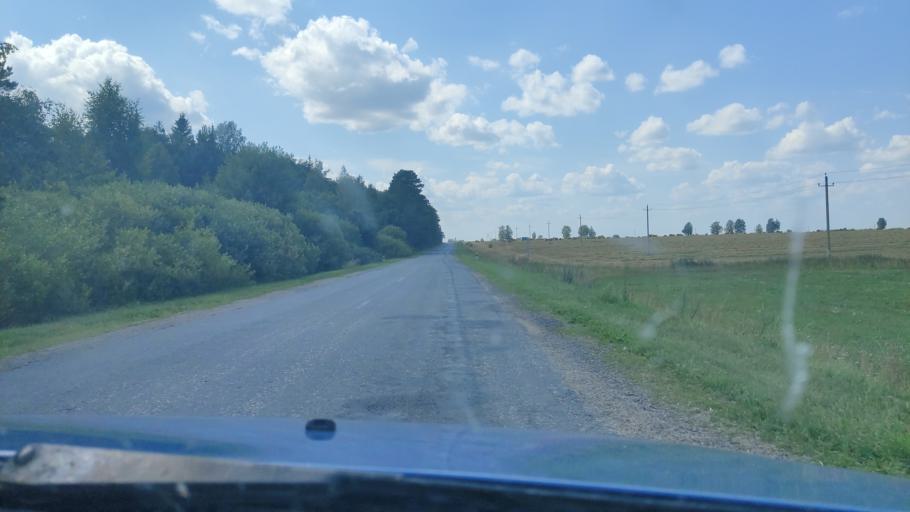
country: BY
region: Vitebsk
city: Dokshytsy
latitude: 54.9241
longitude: 27.8724
